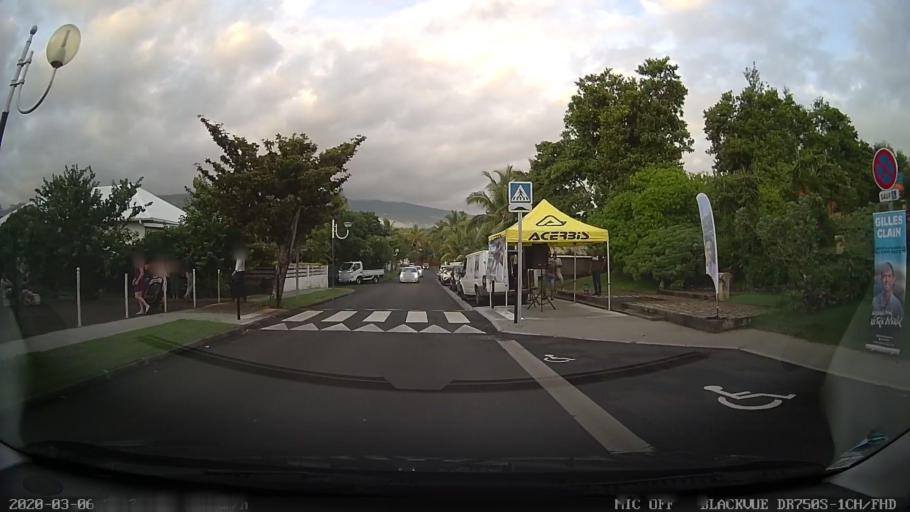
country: RE
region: Reunion
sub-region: Reunion
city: Les Avirons
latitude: -21.2724
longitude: 55.3371
